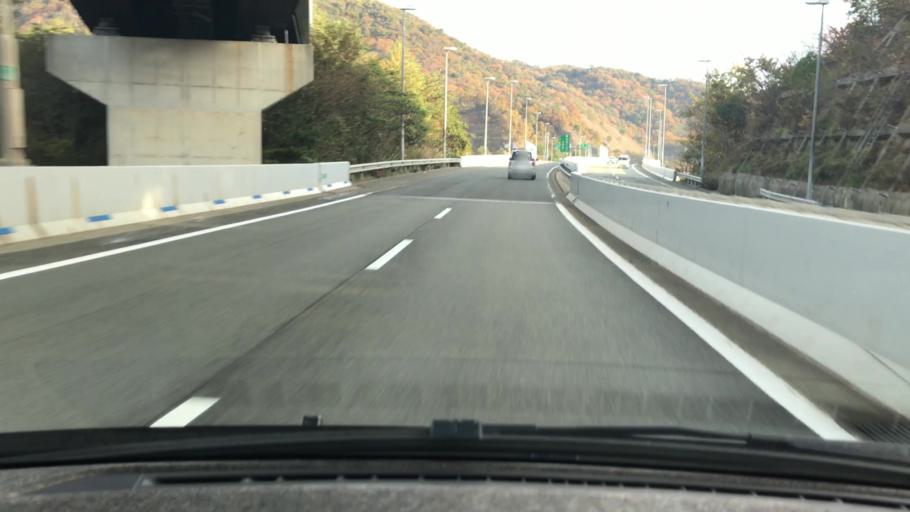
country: JP
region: Hyogo
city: Sandacho
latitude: 34.7951
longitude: 135.2271
